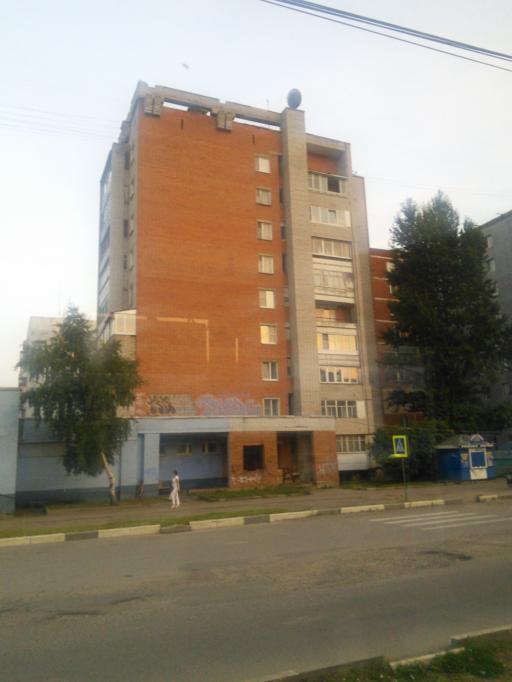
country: RU
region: Jaroslavl
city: Yaroslavl
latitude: 57.7009
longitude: 39.7707
